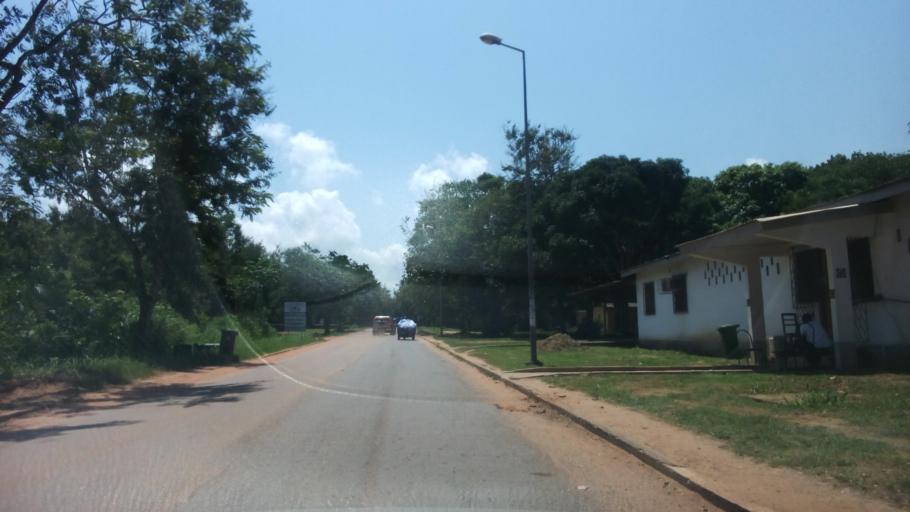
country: GH
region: Central
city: Cape Coast
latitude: 5.1220
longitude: -1.2914
